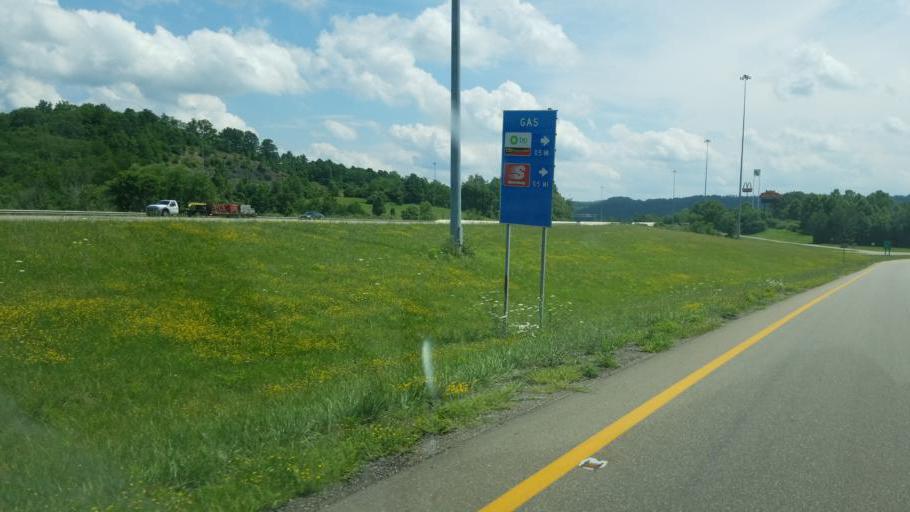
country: US
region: Ohio
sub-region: Tuscarawas County
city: Newcomerstown
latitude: 40.2931
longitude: -81.5580
